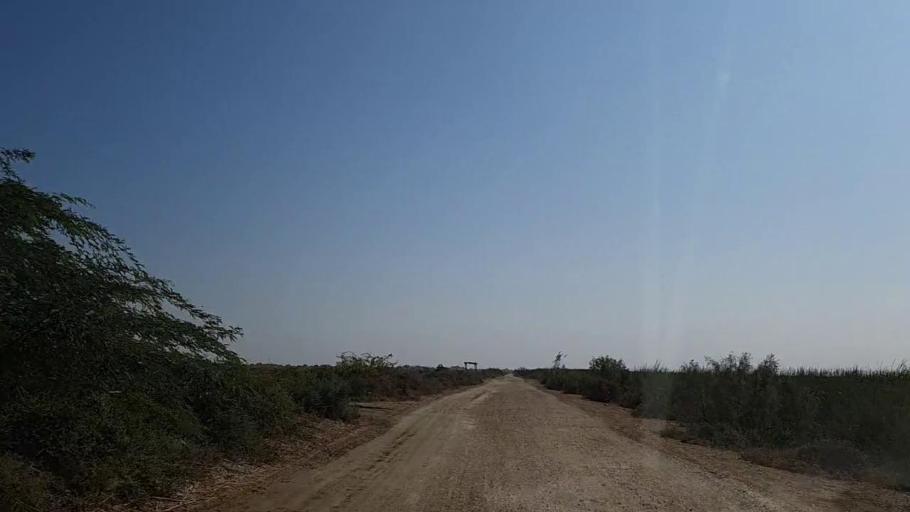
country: PK
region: Sindh
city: Chuhar Jamali
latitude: 24.4681
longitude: 68.0949
